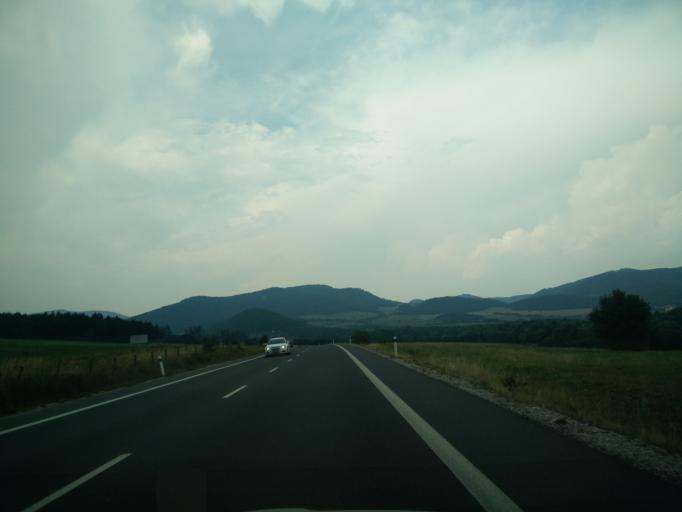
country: SK
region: Banskobystricky
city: Ziar nad Hronom
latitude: 48.6351
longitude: 18.7764
